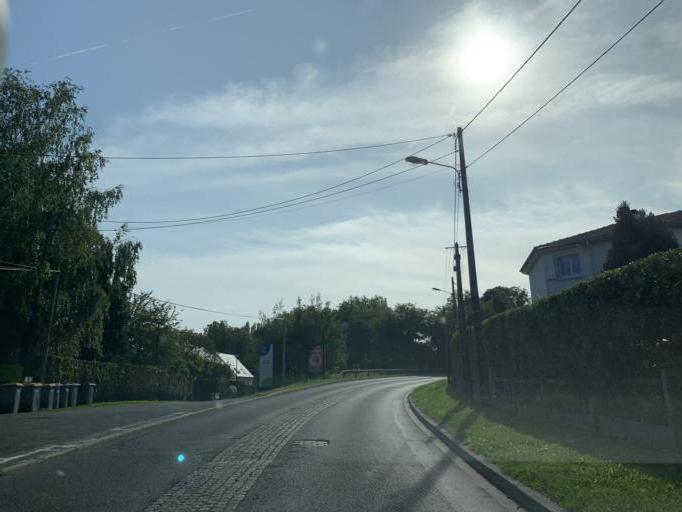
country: FR
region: Ile-de-France
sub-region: Departement de Seine-et-Marne
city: Claye-Souilly
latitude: 48.9406
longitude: 2.6952
